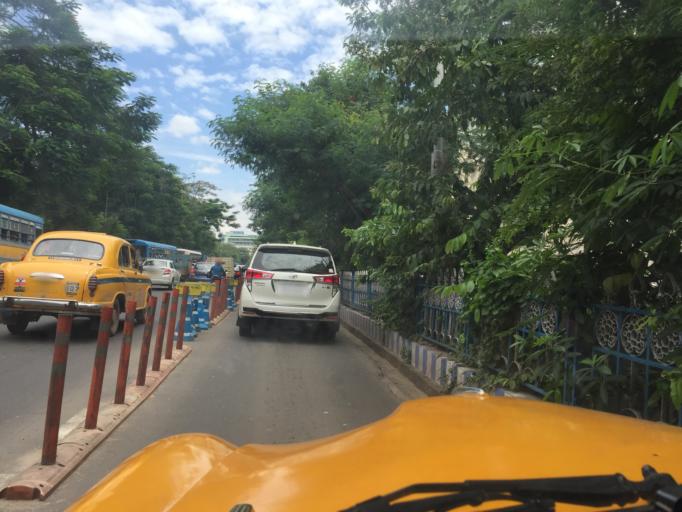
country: IN
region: West Bengal
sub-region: Kolkata
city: Bara Bazar
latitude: 22.5611
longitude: 88.3507
